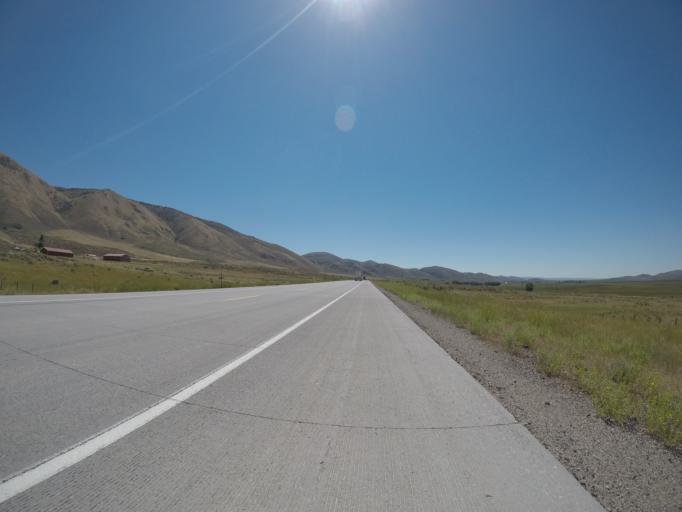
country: US
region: Idaho
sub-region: Bear Lake County
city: Montpelier
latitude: 42.1771
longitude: -111.0017
